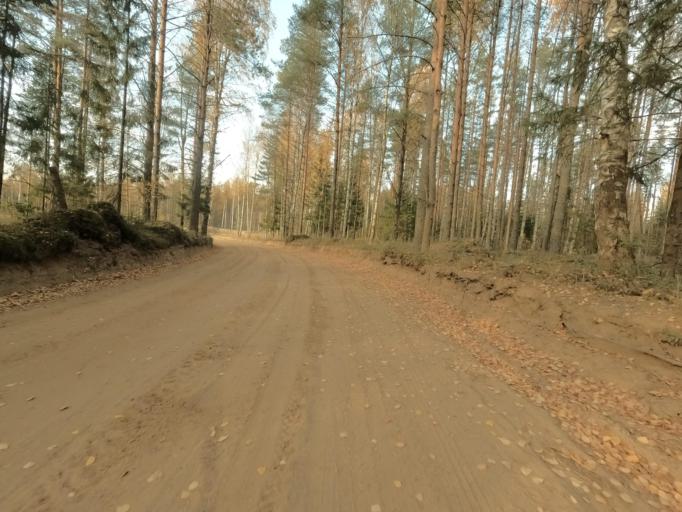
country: RU
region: Leningrad
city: Priladozhskiy
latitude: 59.7381
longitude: 31.3176
